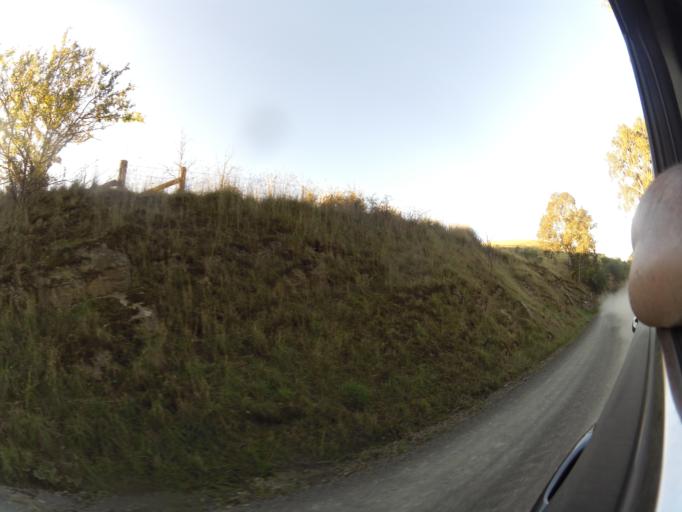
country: AU
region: Victoria
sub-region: Murrindindi
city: Alexandra
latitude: -37.1540
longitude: 145.5348
